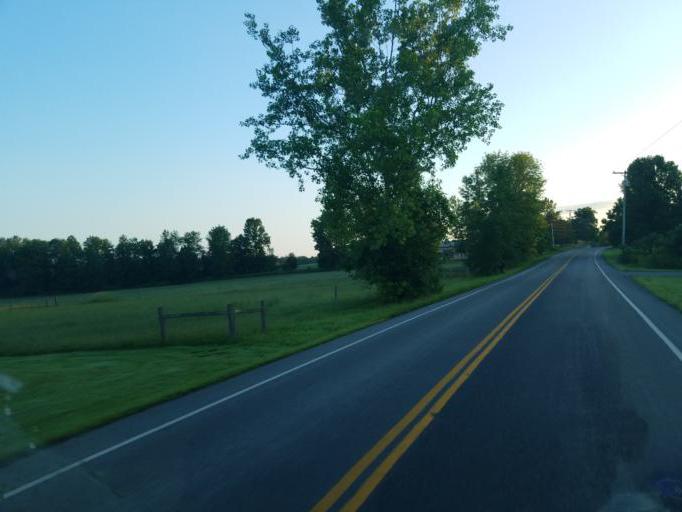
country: US
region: New York
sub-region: Wayne County
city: Clyde
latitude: 43.0777
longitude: -76.8918
